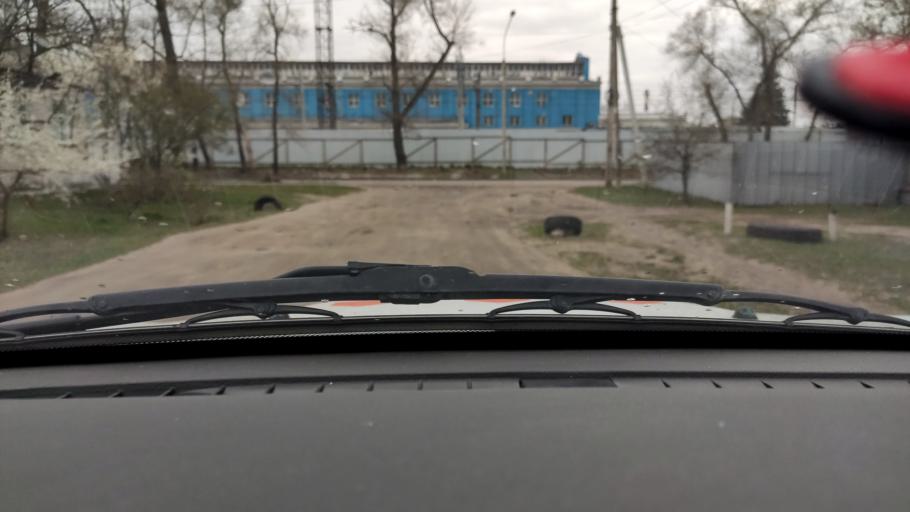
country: RU
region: Voronezj
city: Somovo
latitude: 51.7301
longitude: 39.2707
